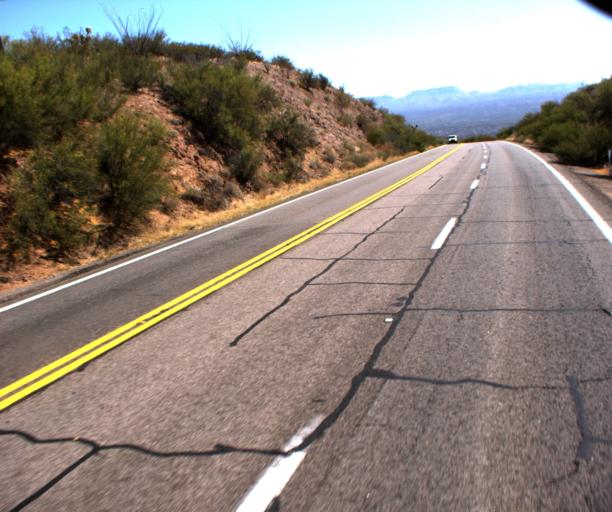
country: US
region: Arizona
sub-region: Pinal County
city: Mammoth
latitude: 32.6744
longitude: -110.6601
